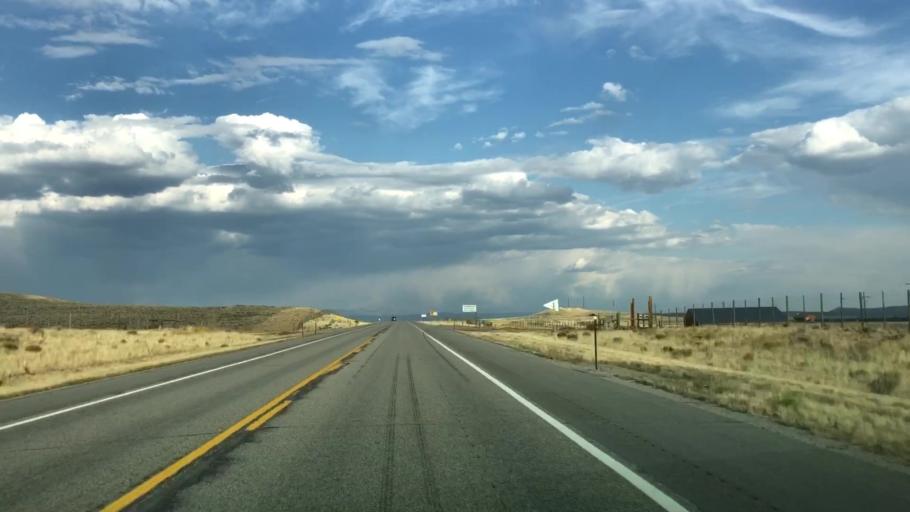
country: US
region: Wyoming
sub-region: Sublette County
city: Pinedale
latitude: 42.8894
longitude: -110.0581
